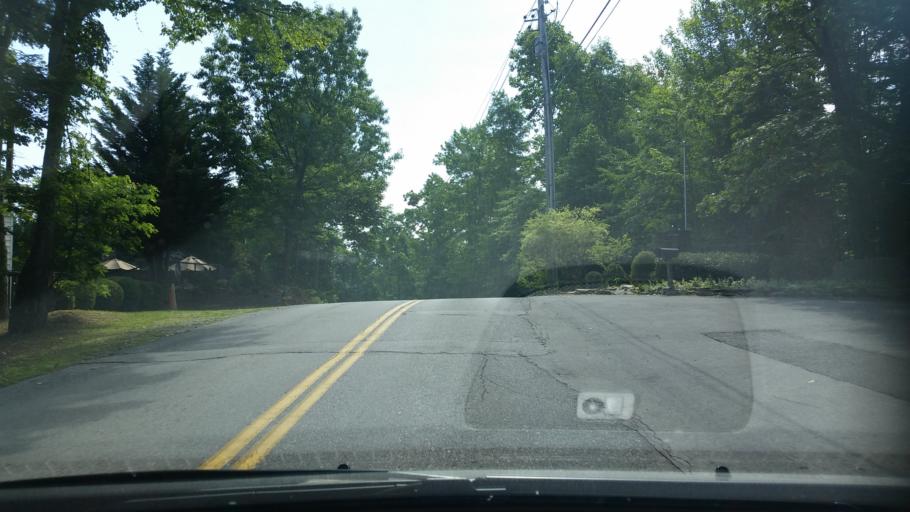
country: US
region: Tennessee
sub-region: Sevier County
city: Gatlinburg
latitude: 35.7122
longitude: -83.5353
